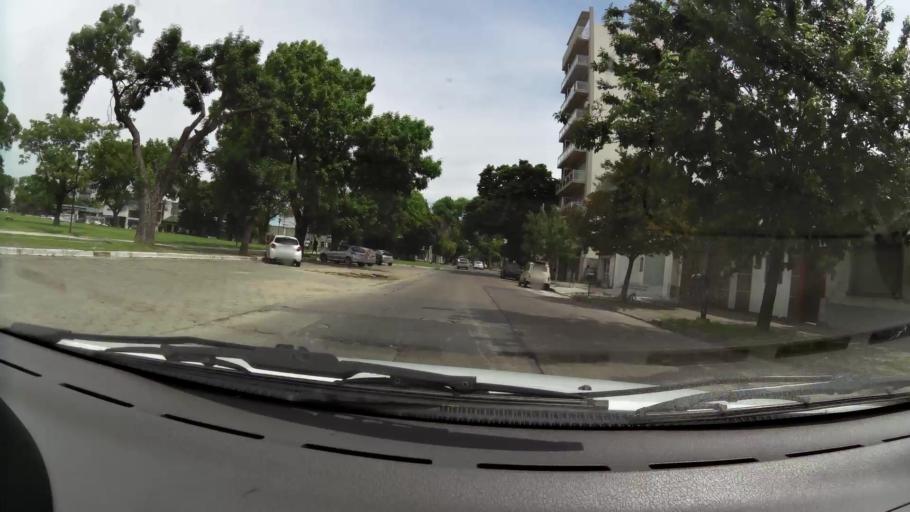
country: AR
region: Buenos Aires
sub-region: Partido de La Plata
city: La Plata
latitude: -34.9424
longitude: -57.9550
